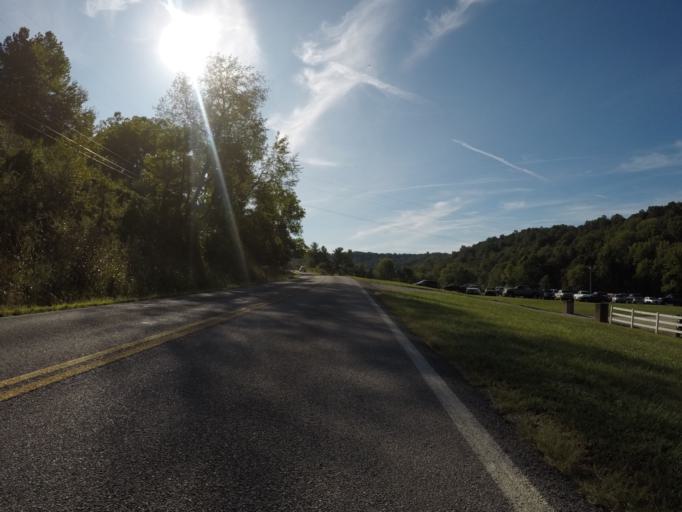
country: US
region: Ohio
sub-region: Lawrence County
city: Burlington
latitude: 38.4977
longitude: -82.5040
